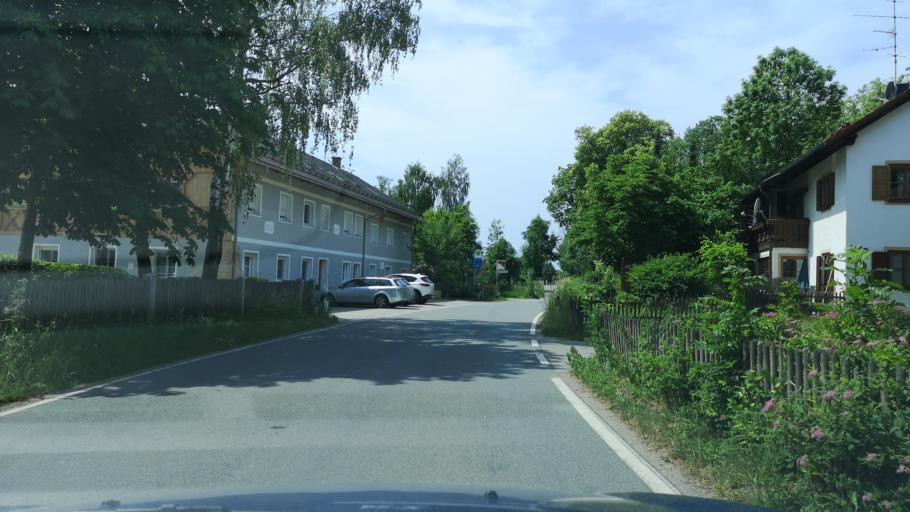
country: DE
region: Bavaria
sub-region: Upper Bavaria
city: Anzing
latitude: 48.1380
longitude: 11.8467
